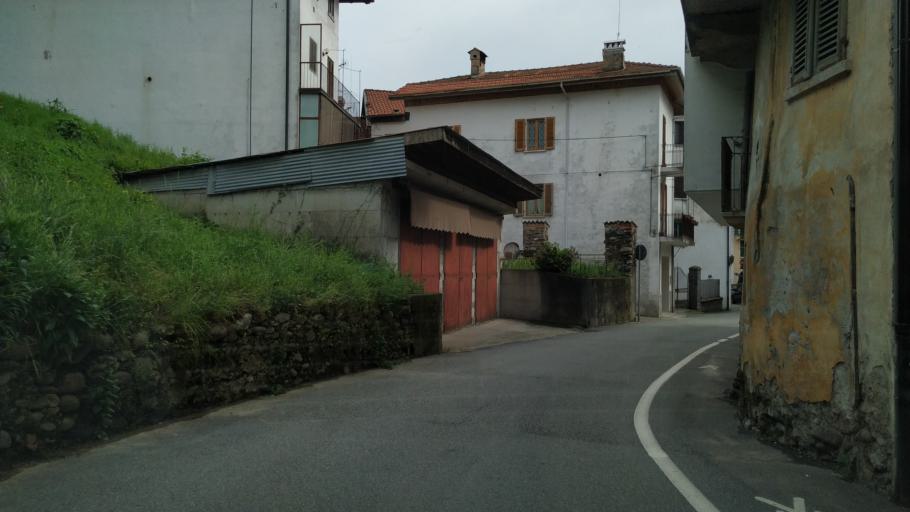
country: IT
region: Piedmont
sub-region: Provincia di Novara
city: Grignasco
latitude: 45.6862
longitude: 8.3381
